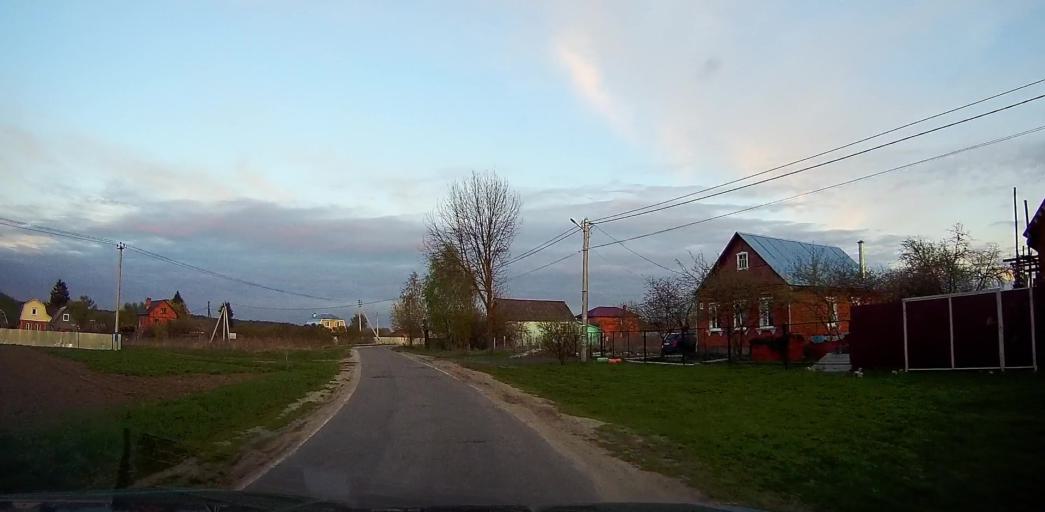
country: RU
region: Moskovskaya
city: Peski
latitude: 55.2119
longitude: 38.7398
